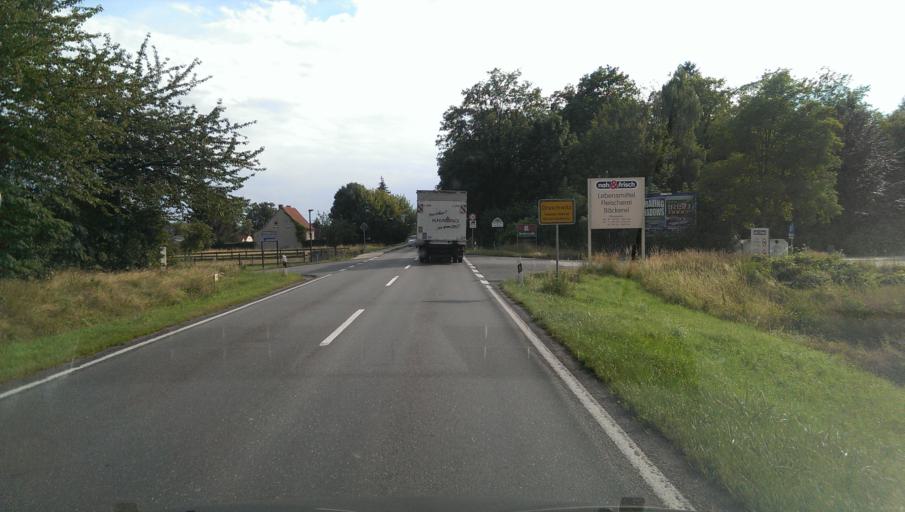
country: DE
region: Saxony-Anhalt
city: Zeitz
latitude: 51.1021
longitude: 12.1824
